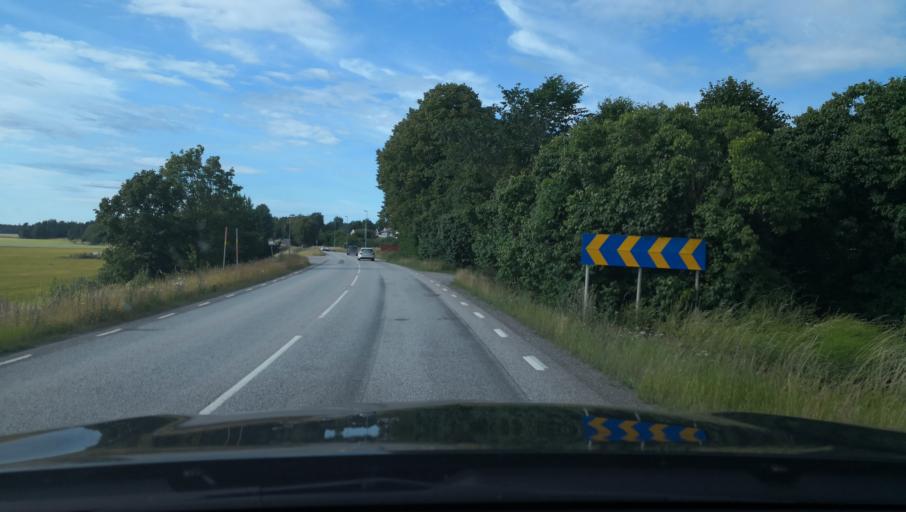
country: SE
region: Uppsala
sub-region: Habo Kommun
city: Balsta
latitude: 59.5938
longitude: 17.5109
